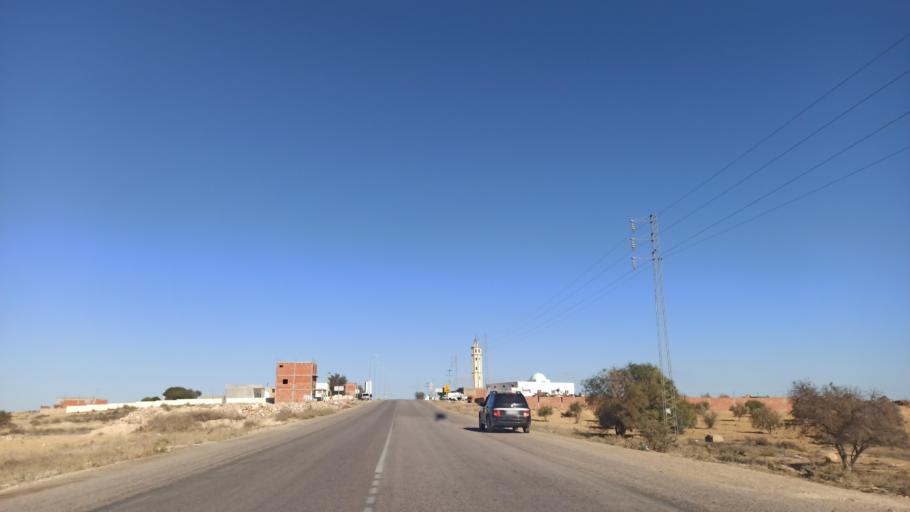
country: TN
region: Sidi Bu Zayd
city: Jilma
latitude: 35.2580
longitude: 9.4024
